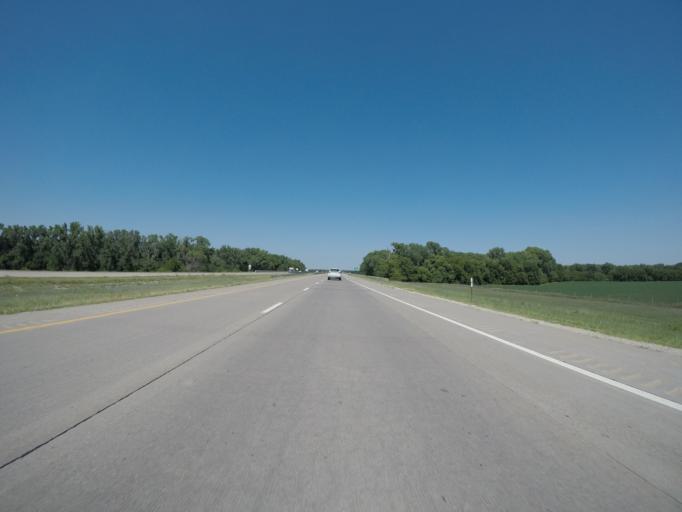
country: US
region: Kansas
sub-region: Saline County
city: Salina
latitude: 38.8844
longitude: -97.5884
